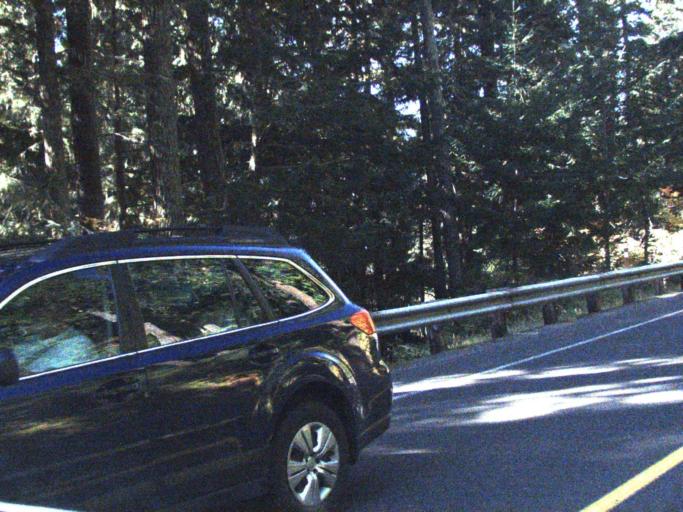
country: US
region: Washington
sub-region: Pierce County
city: Buckley
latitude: 46.6710
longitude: -121.4962
